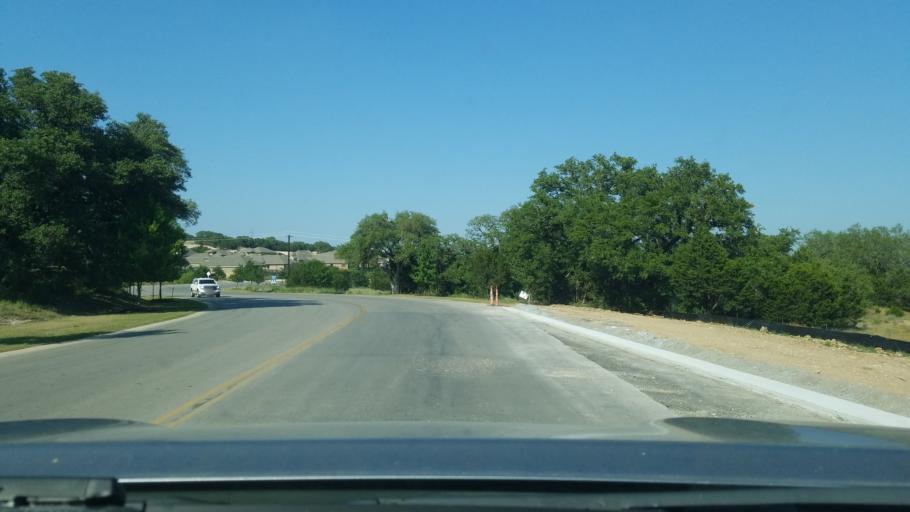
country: US
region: Texas
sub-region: Comal County
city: Bulverde
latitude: 29.7700
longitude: -98.4188
